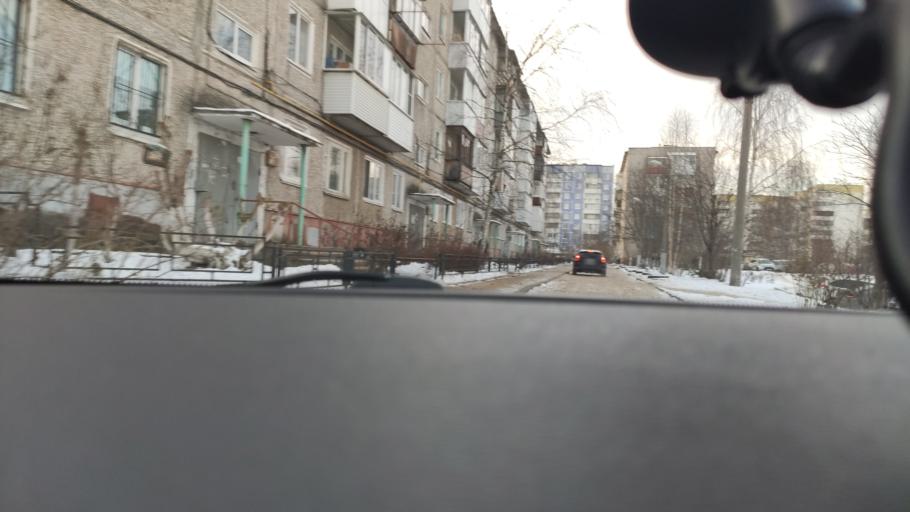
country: RU
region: Perm
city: Perm
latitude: 58.1122
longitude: 56.2832
